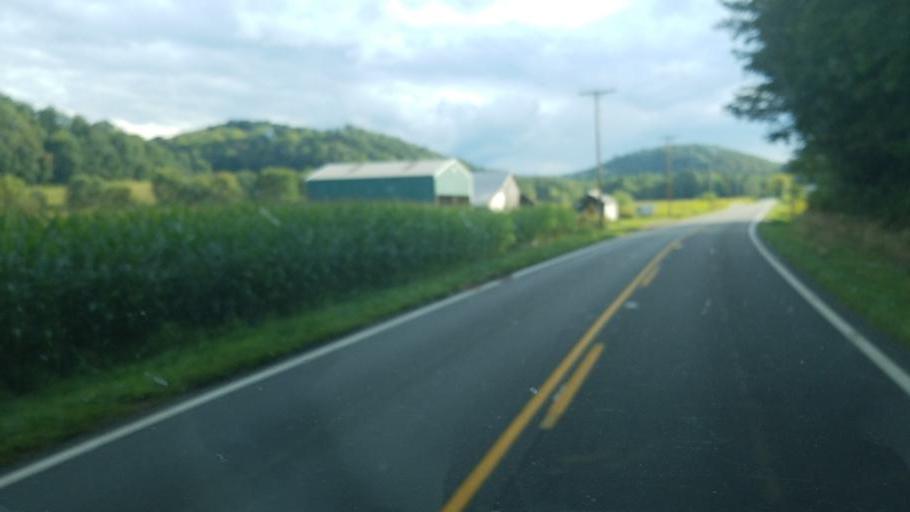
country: US
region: Ohio
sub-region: Holmes County
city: Millersburg
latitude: 40.4730
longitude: -82.0646
